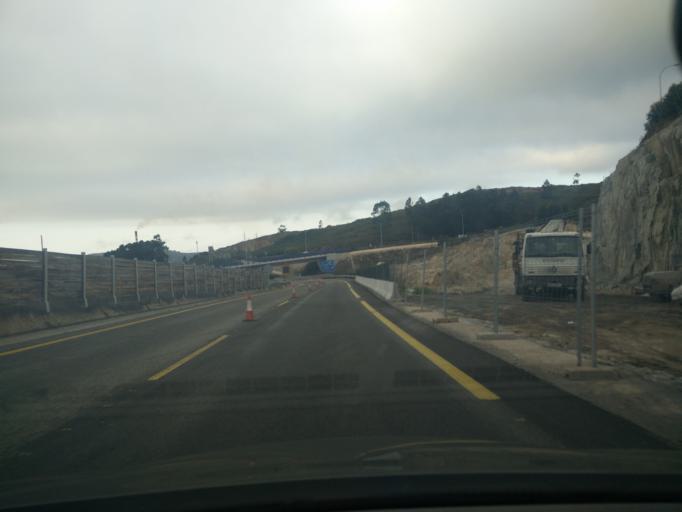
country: ES
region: Galicia
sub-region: Provincia da Coruna
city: Arteixo
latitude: 43.3326
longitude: -8.4553
